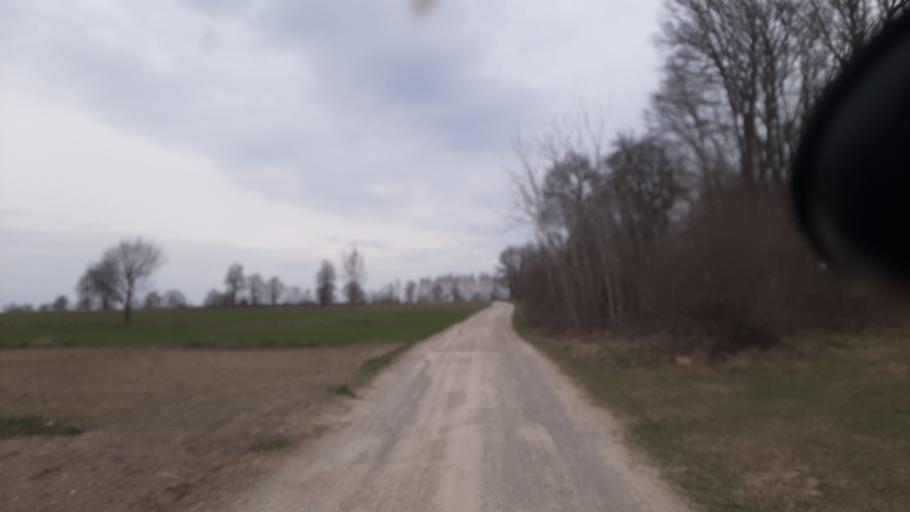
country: PL
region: Lublin Voivodeship
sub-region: Powiat lubartowski
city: Abramow
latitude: 51.4470
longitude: 22.3354
